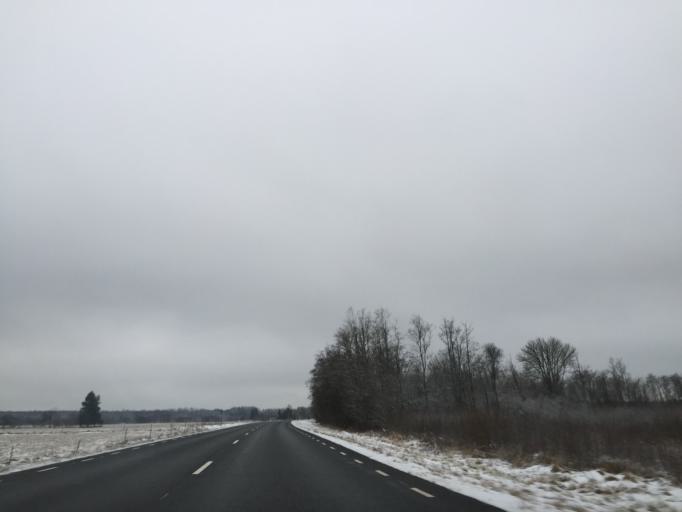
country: EE
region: Laeaene
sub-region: Lihula vald
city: Lihula
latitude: 58.6627
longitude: 23.8353
